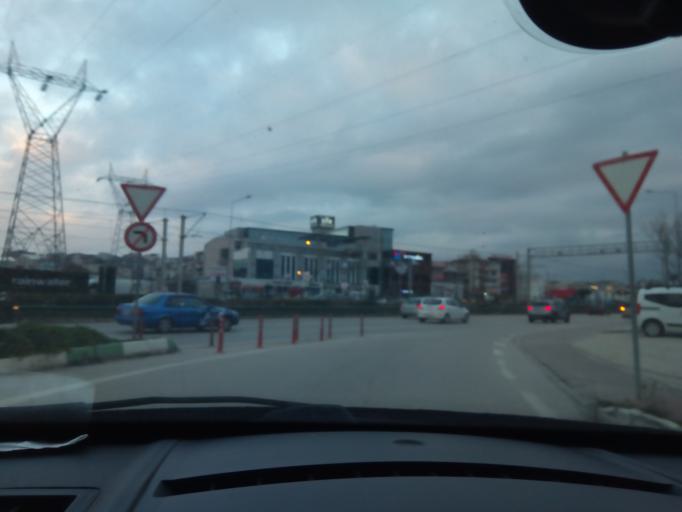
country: TR
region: Bursa
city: Niluefer
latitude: 40.2379
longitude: 28.9738
